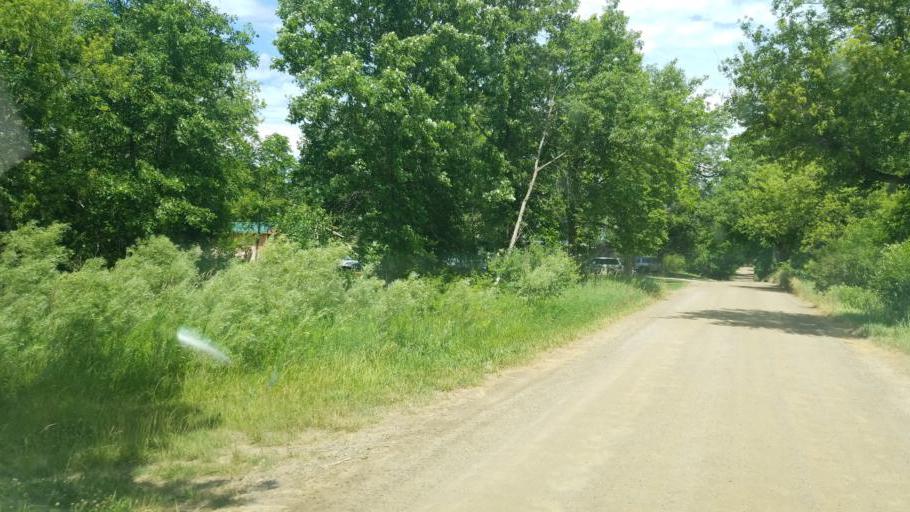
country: US
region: Michigan
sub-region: Eaton County
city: Charlotte
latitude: 42.6203
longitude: -84.8855
